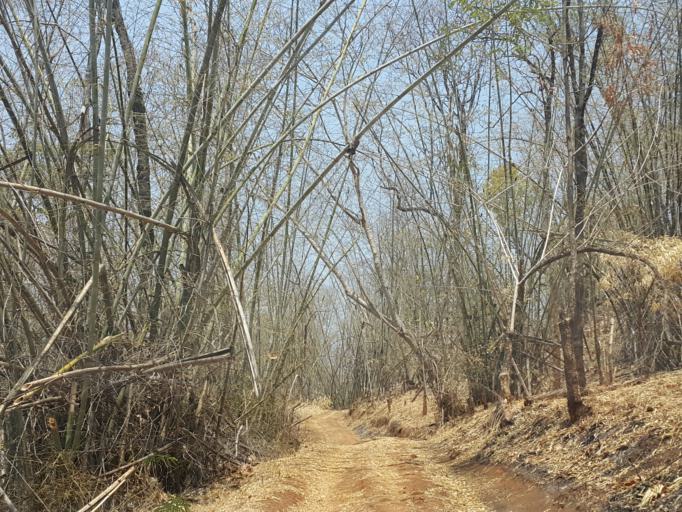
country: TH
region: Chiang Mai
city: Samoeng
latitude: 18.7880
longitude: 98.8249
